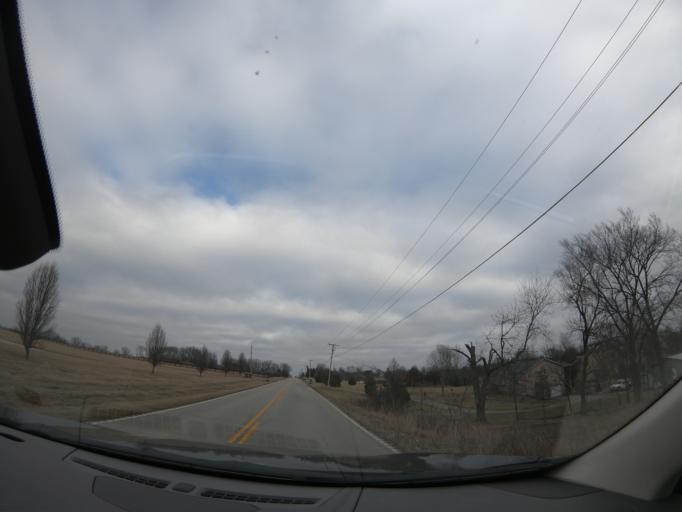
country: US
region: Kentucky
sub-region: Nelson County
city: Bardstown
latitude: 37.8344
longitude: -85.3972
